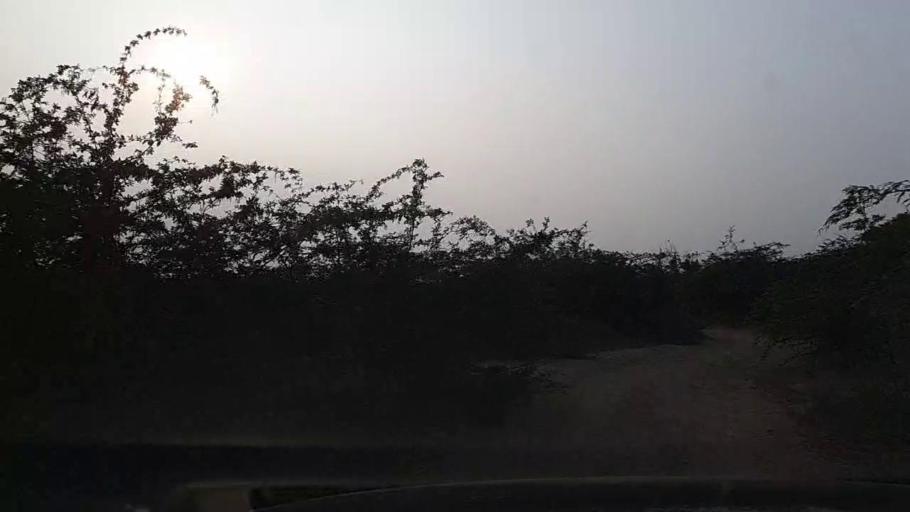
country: PK
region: Sindh
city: Gharo
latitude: 24.7801
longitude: 67.7115
